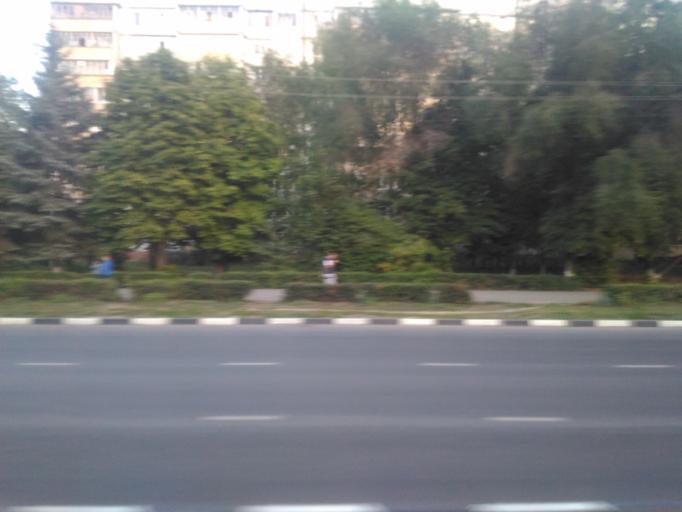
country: RU
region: Ulyanovsk
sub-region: Ulyanovskiy Rayon
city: Ulyanovsk
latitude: 54.2835
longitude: 48.3001
